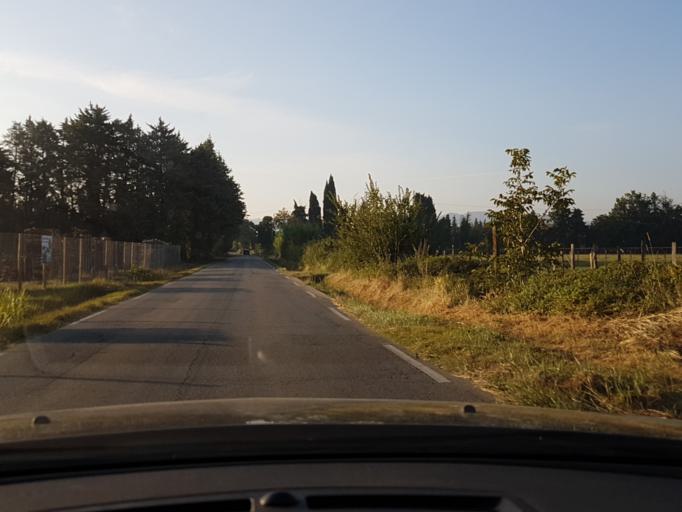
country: FR
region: Provence-Alpes-Cote d'Azur
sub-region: Departement des Bouches-du-Rhone
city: Molleges
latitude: 43.7978
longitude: 4.9532
